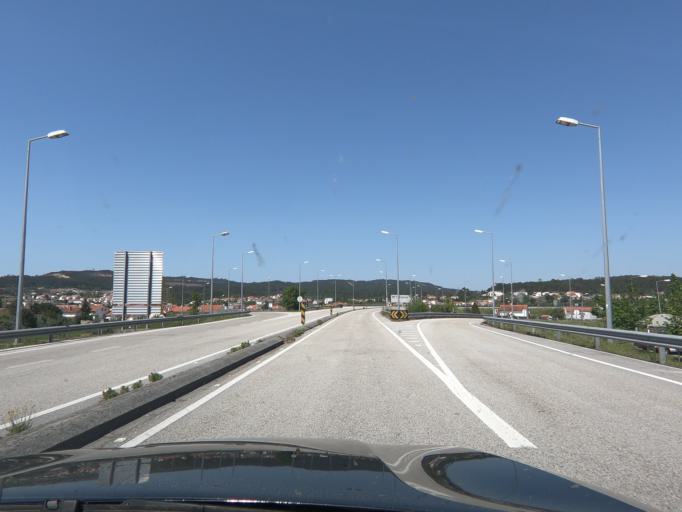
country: PT
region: Coimbra
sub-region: Miranda do Corvo
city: Miranda do Corvo
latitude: 40.0856
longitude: -8.3238
